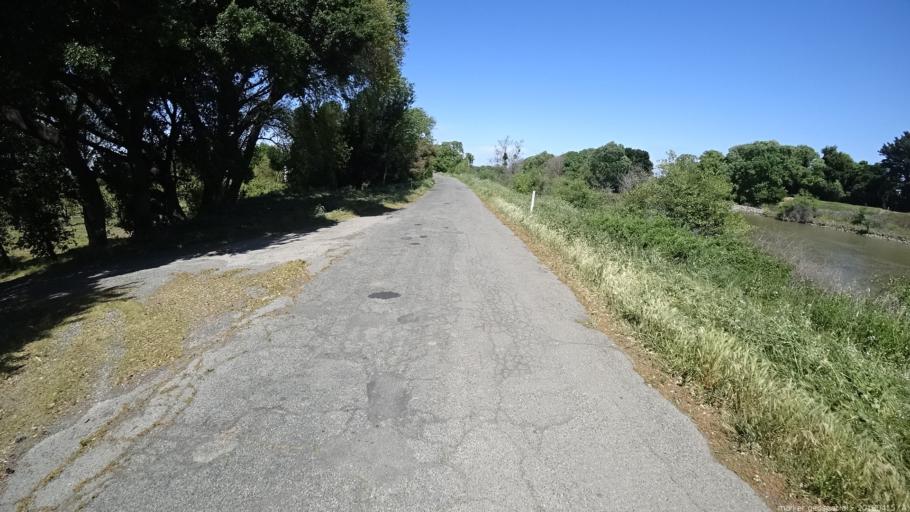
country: US
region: California
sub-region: Sacramento County
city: Walnut Grove
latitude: 38.2881
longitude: -121.5841
